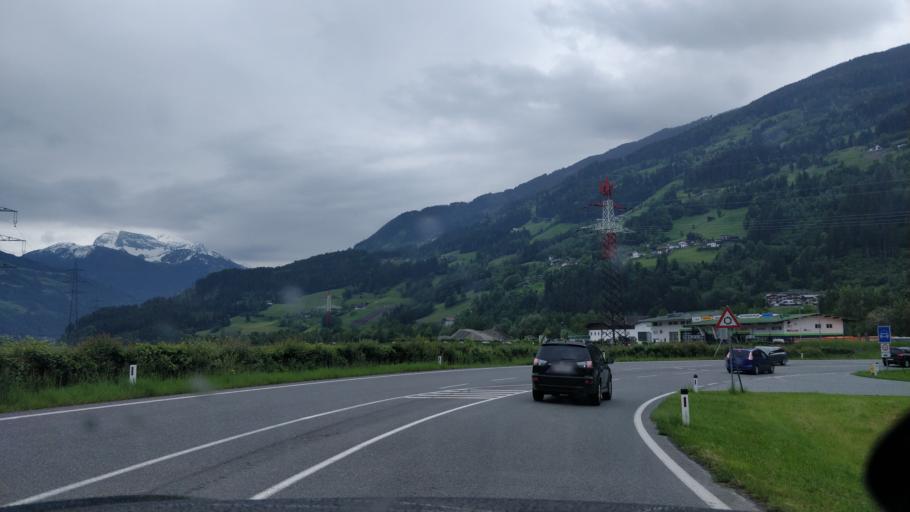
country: AT
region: Tyrol
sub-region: Politischer Bezirk Schwaz
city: Stumm
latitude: 47.2909
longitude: 11.8815
